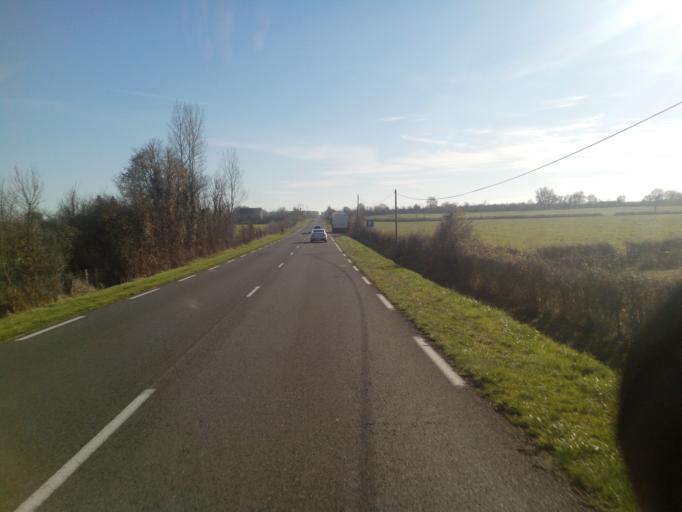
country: FR
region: Poitou-Charentes
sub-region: Departement de la Vienne
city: Lussac-les-Chateaux
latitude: 46.3720
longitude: 0.7618
